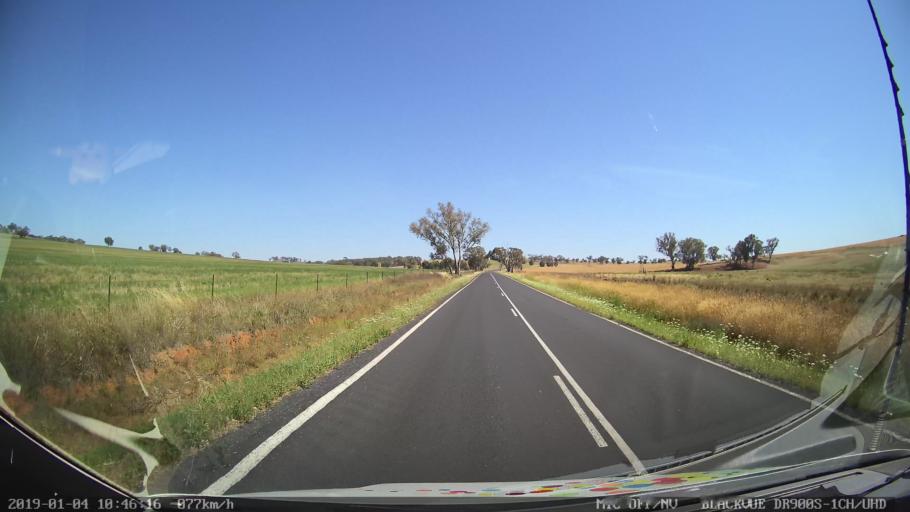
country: AU
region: New South Wales
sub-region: Cabonne
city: Molong
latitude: -33.2835
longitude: 148.7242
